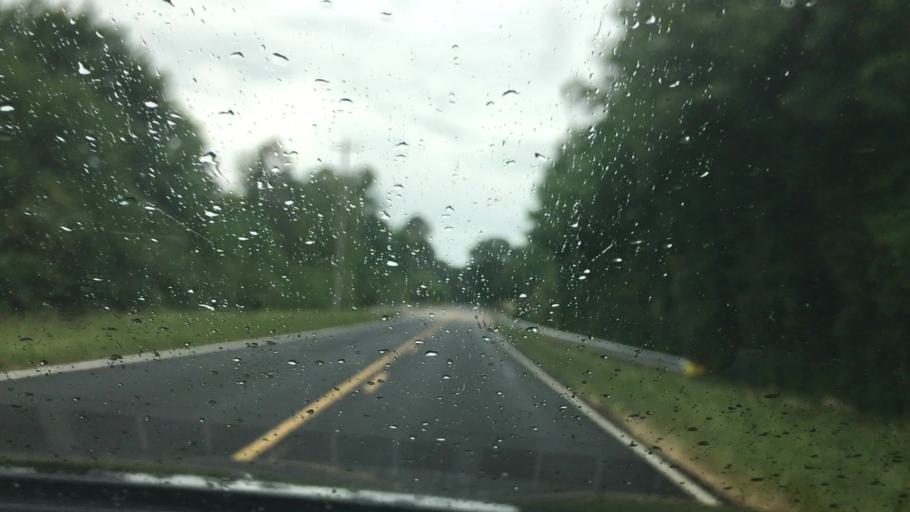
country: US
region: North Carolina
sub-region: Stanly County
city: Badin
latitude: 35.3650
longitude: -80.1159
